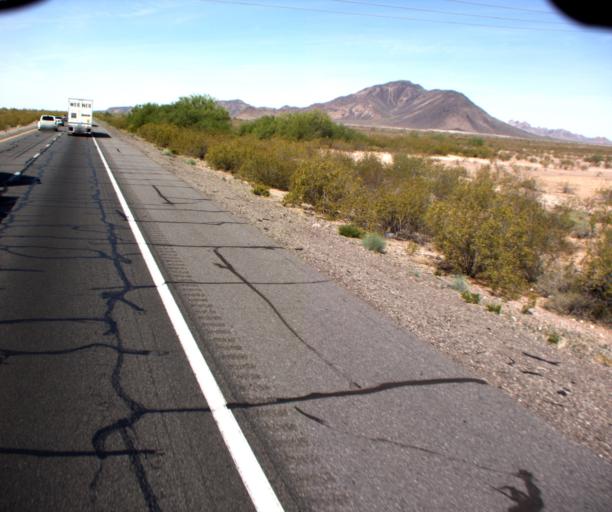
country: US
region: Arizona
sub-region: Maricopa County
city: Buckeye
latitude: 33.5142
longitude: -113.0303
